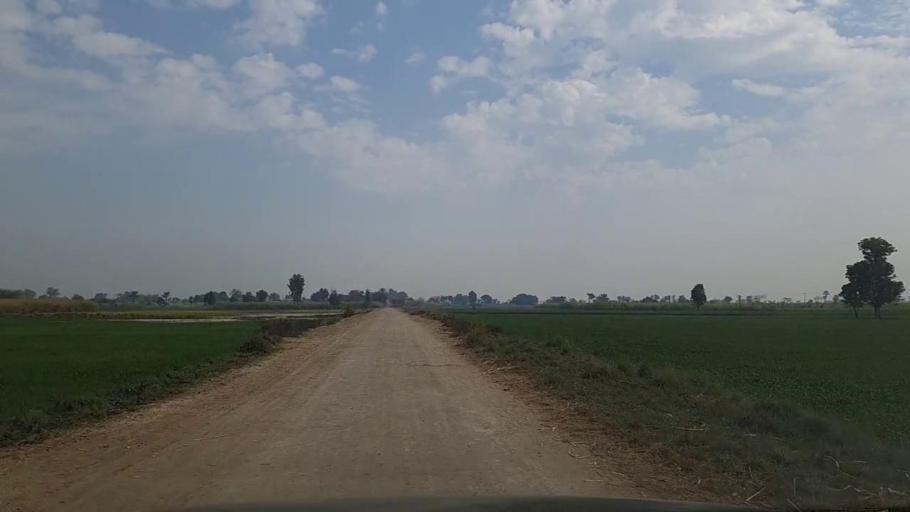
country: PK
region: Sindh
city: Daur
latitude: 26.3985
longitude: 68.3505
